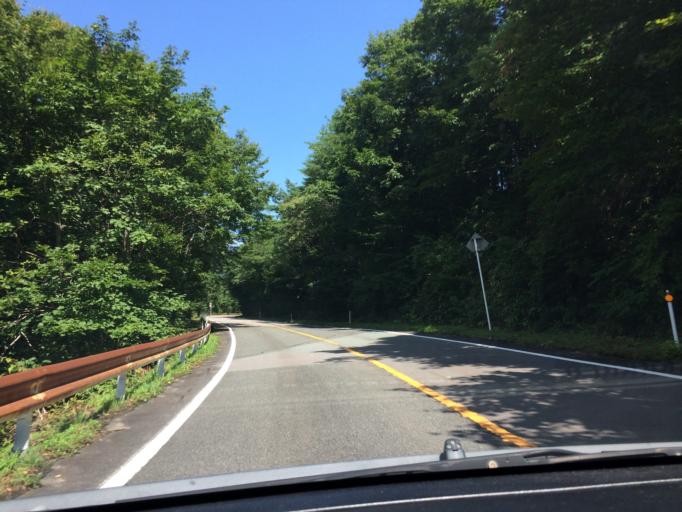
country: JP
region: Tottori
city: Kurayoshi
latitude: 35.3198
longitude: 133.6060
